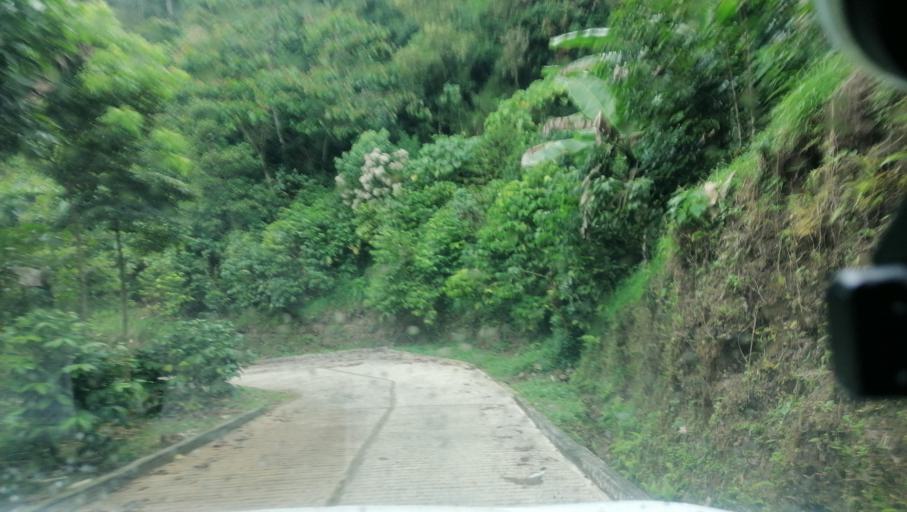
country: MX
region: Chiapas
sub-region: Cacahoatan
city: Benito Juarez
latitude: 15.0951
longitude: -92.1586
